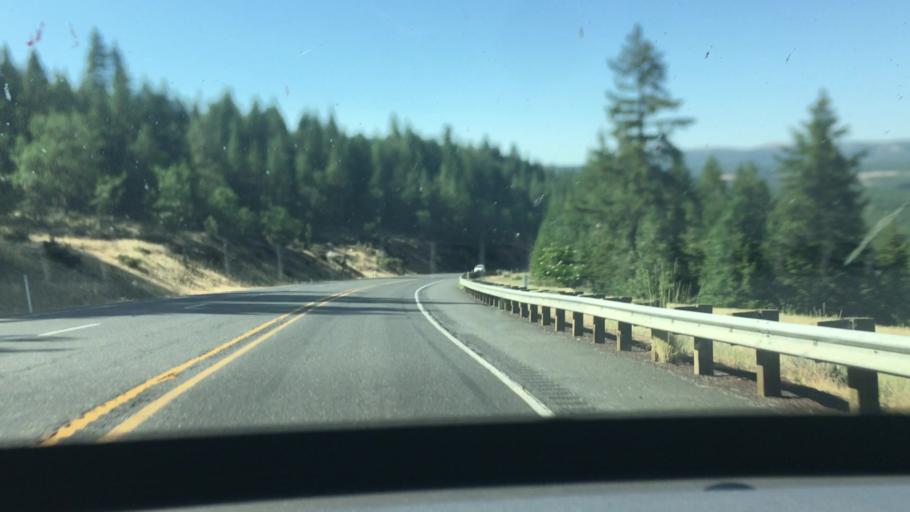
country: US
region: Washington
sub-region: Klickitat County
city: Goldendale
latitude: 45.9040
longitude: -120.7119
